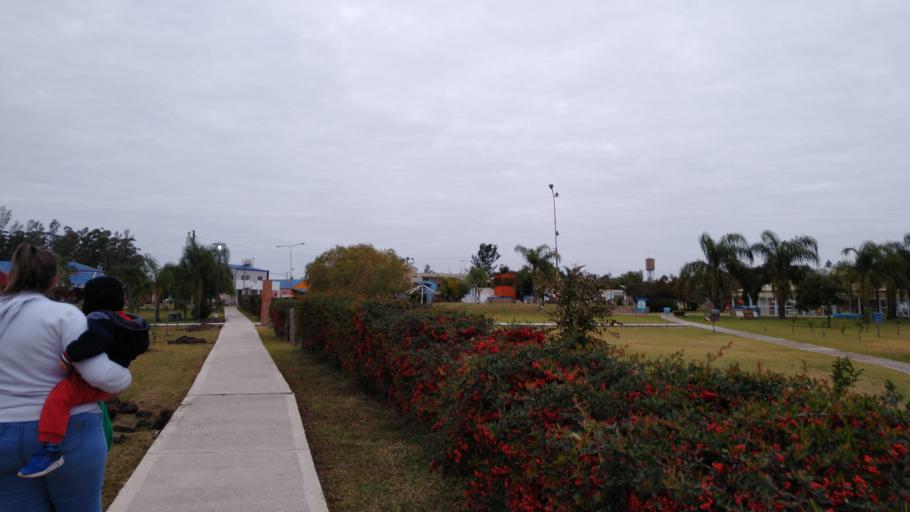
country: AR
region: Entre Rios
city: Chajari
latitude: -30.7442
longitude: -58.0132
